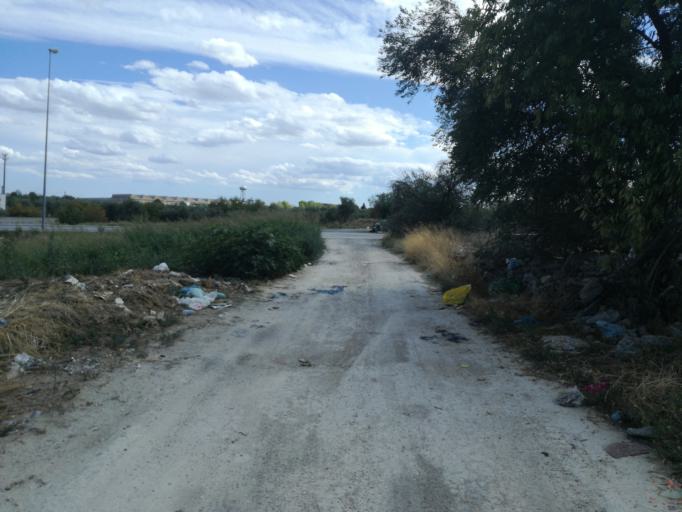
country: IT
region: Apulia
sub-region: Provincia di Bari
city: Triggiano
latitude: 41.0645
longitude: 16.9322
